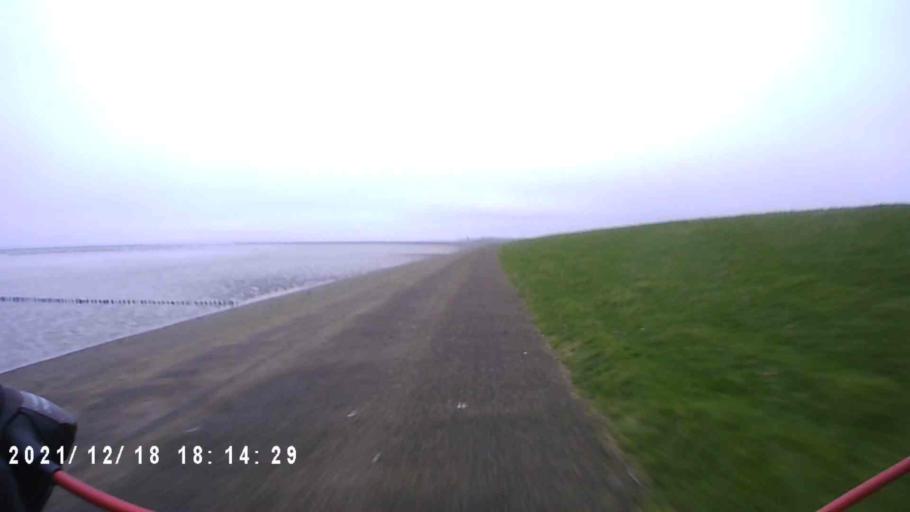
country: NL
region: Friesland
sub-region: Gemeente Dongeradeel
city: Ternaard
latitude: 53.3935
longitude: 5.9596
